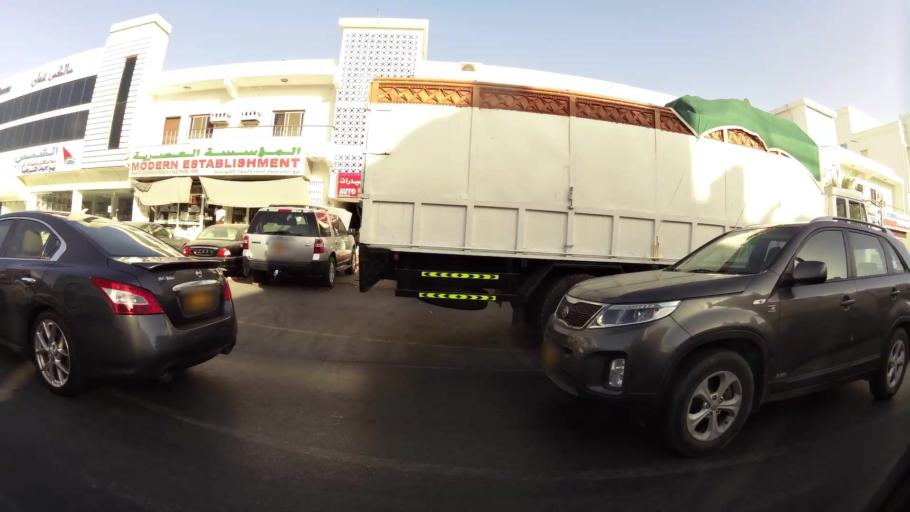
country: OM
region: Muhafazat Masqat
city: Muscat
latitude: 23.5876
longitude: 58.5512
